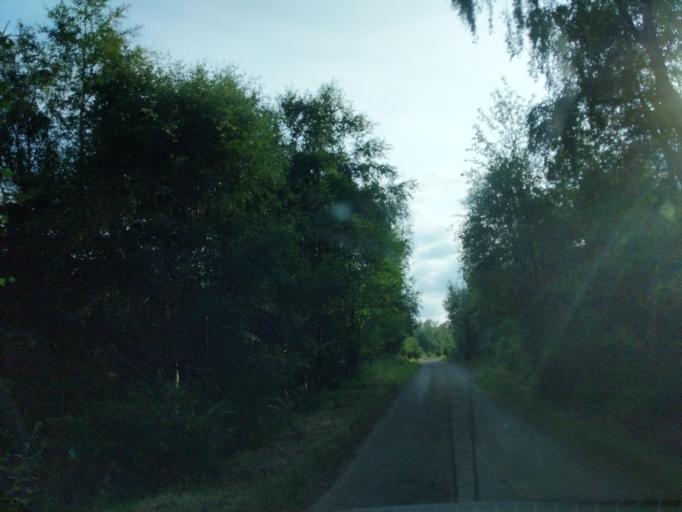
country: GB
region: Scotland
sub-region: Moray
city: Dufftown
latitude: 57.4767
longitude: -3.0722
